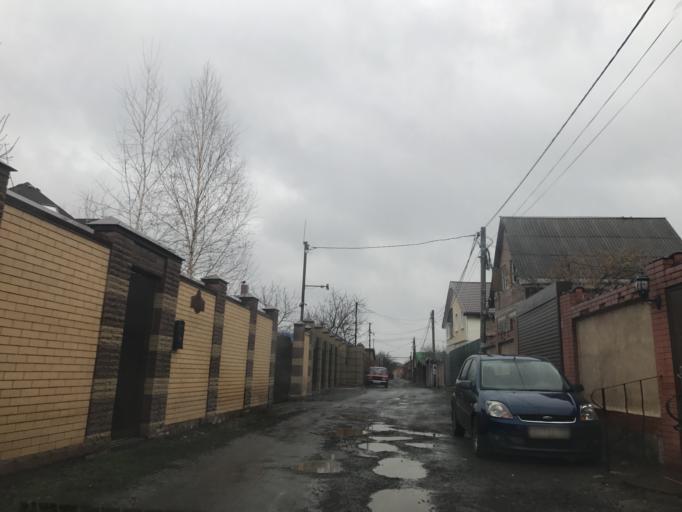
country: RU
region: Rostov
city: Severnyy
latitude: 47.2446
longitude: 39.6179
